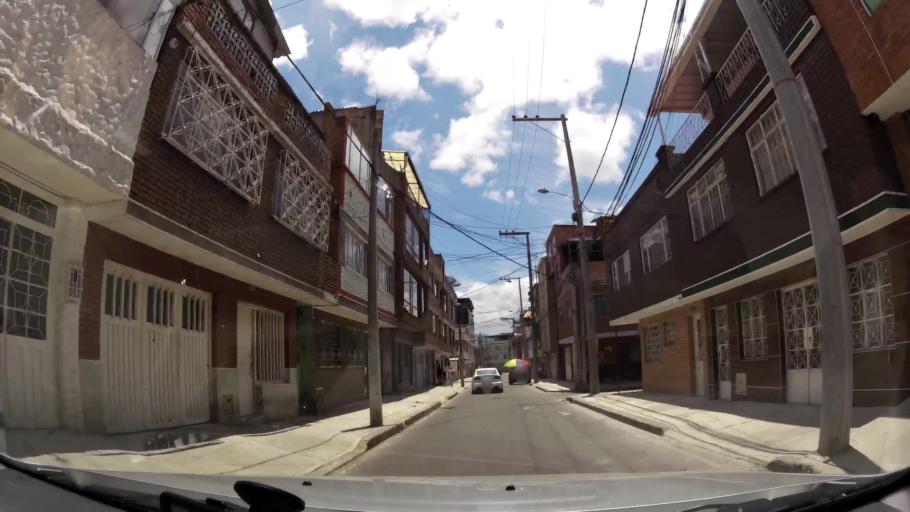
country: CO
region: Bogota D.C.
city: Bogota
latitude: 4.5855
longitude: -74.1079
